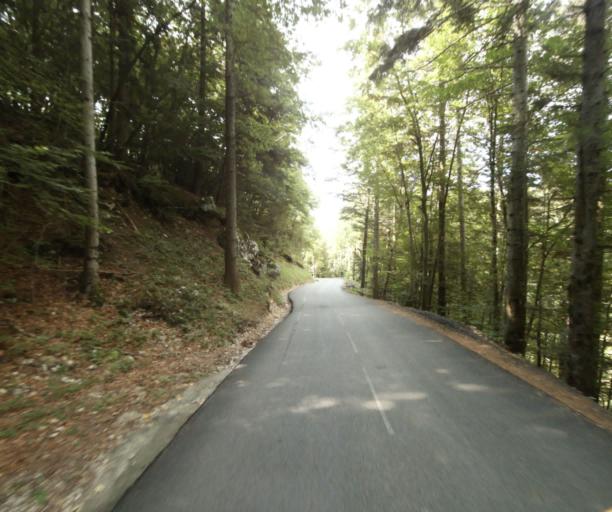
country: FR
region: Rhone-Alpes
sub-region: Departement de l'Isere
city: Le Sappey-en-Chartreuse
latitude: 45.2701
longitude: 5.7534
